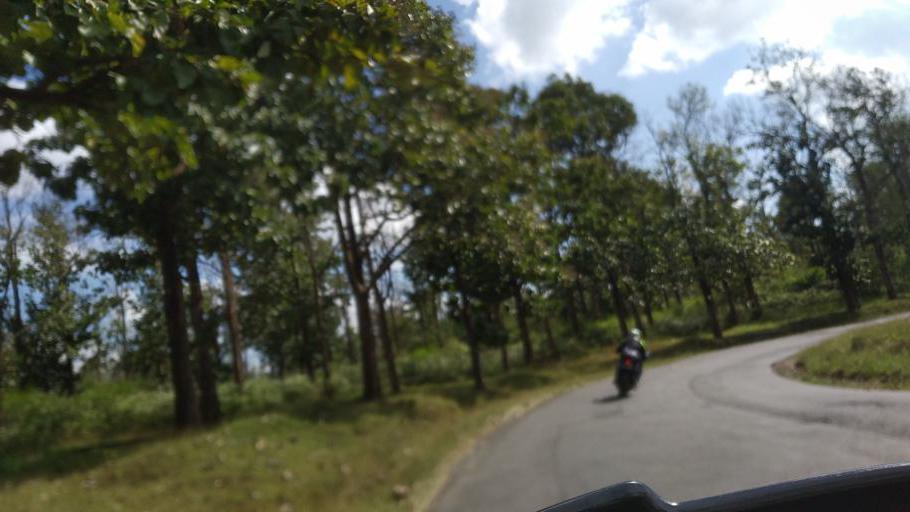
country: IN
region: Kerala
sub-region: Wayanad
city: Panamaram
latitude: 11.9197
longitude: 76.0665
